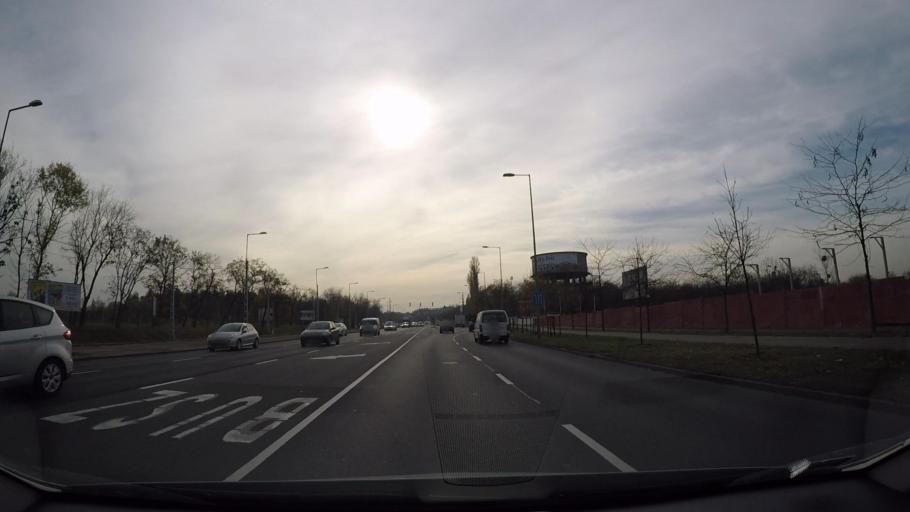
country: HU
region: Budapest
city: Budapest X. keruelet
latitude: 47.4984
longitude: 19.1375
